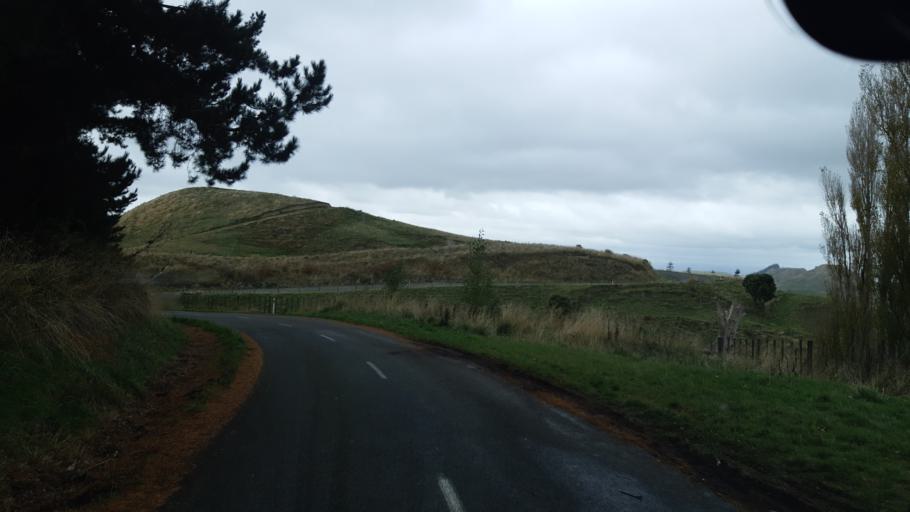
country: NZ
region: Manawatu-Wanganui
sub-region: Ruapehu District
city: Waiouru
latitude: -39.6159
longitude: 175.6482
